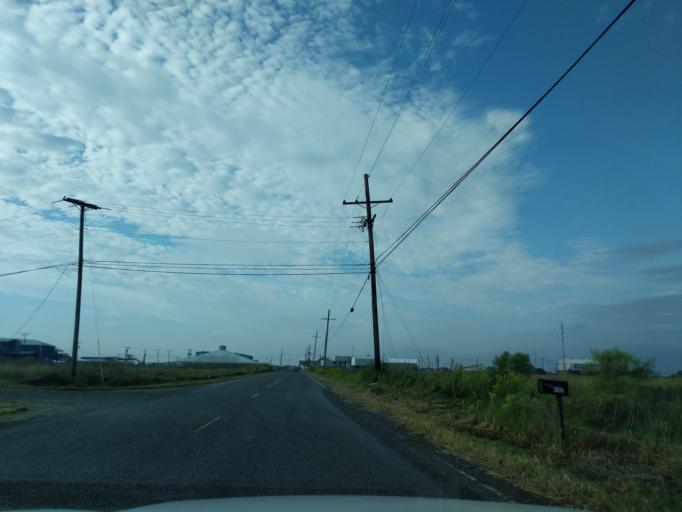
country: US
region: Louisiana
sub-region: Terrebonne Parish
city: Dulac
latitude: 29.2492
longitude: -90.6613
